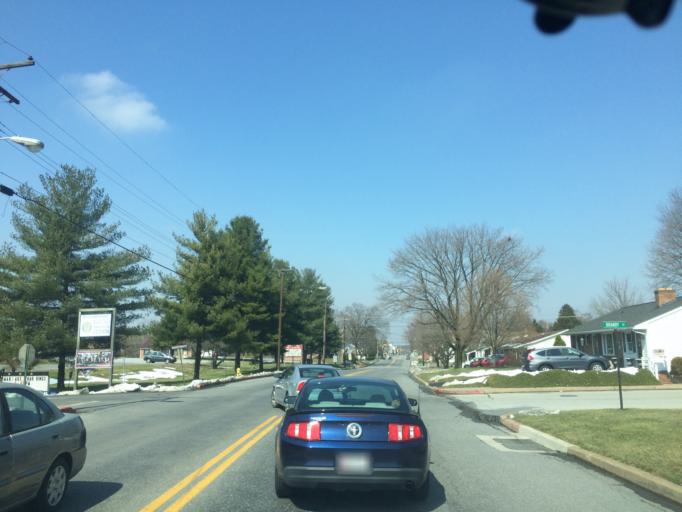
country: US
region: Maryland
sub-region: Washington County
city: Williamsport
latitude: 39.5939
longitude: -77.8211
